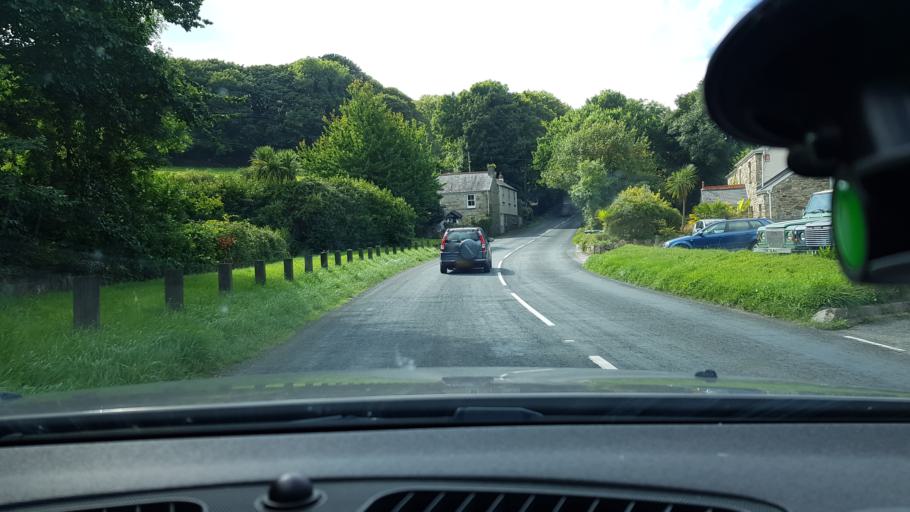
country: GB
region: England
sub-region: Cornwall
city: Penzance
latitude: 50.1069
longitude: -5.5713
